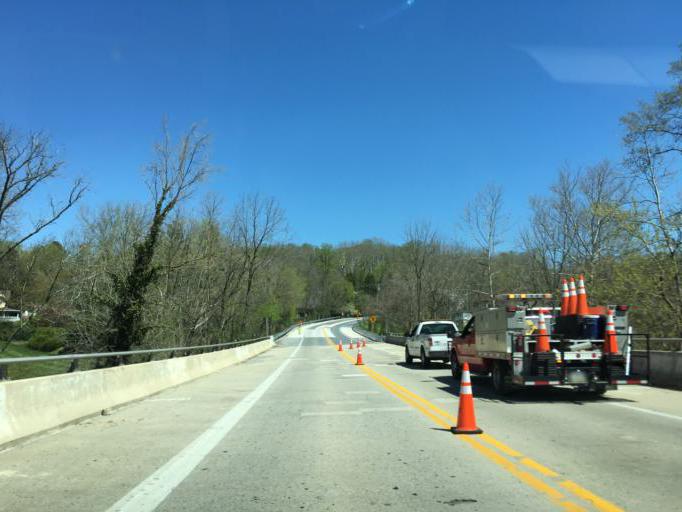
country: US
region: Maryland
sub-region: Baltimore County
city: Hunt Valley
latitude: 39.5787
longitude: -76.6183
